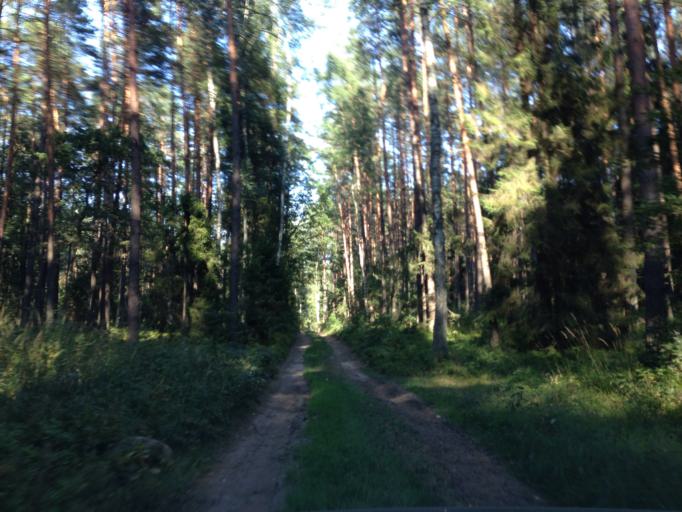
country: PL
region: Kujawsko-Pomorskie
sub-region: Powiat brodnicki
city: Gorzno
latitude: 53.1918
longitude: 19.7071
